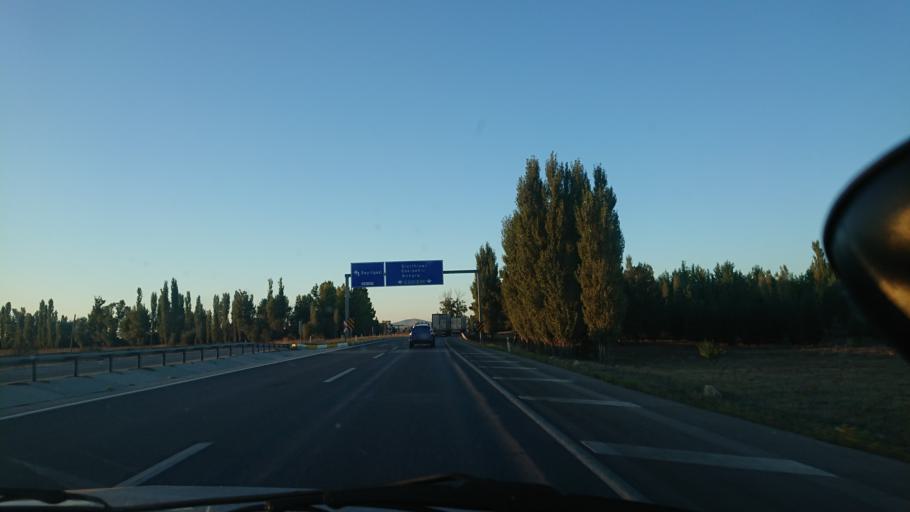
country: TR
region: Eskisehir
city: Mahmudiye
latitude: 39.5679
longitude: 30.9141
